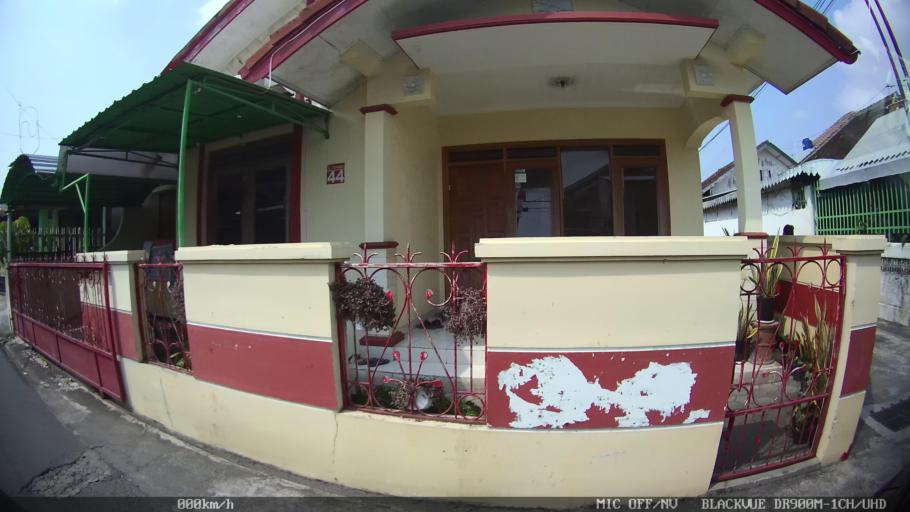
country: ID
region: Daerah Istimewa Yogyakarta
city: Yogyakarta
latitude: -7.8121
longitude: 110.3796
